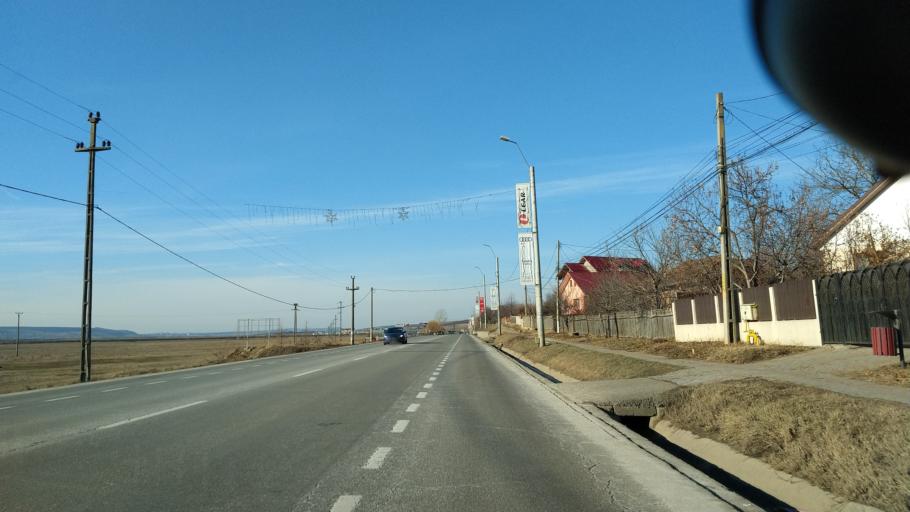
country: RO
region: Iasi
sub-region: Comuna Letcani
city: Letcani
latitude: 47.2002
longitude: 27.3887
